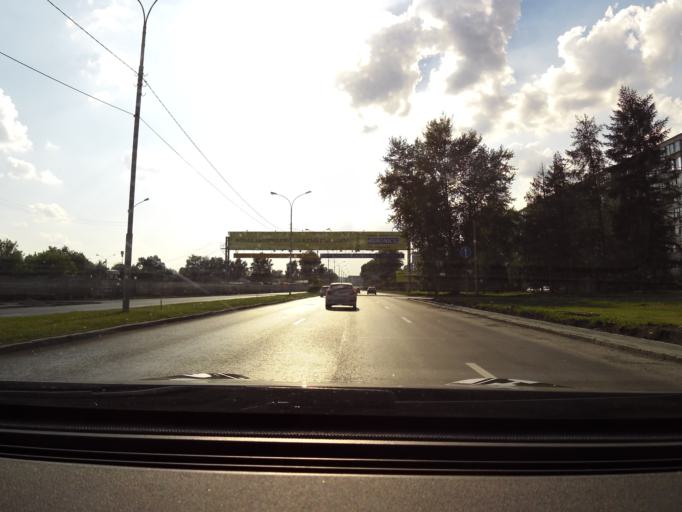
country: RU
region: Sverdlovsk
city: Shirokaya Rechka
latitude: 56.8266
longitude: 60.5406
